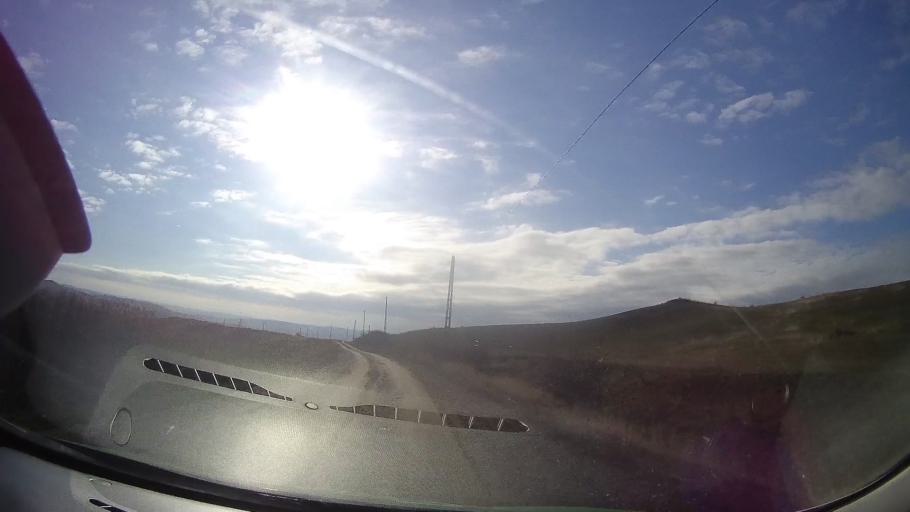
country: RO
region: Mures
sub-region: Comuna Saulia
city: Saulia
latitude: 46.5947
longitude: 24.2195
